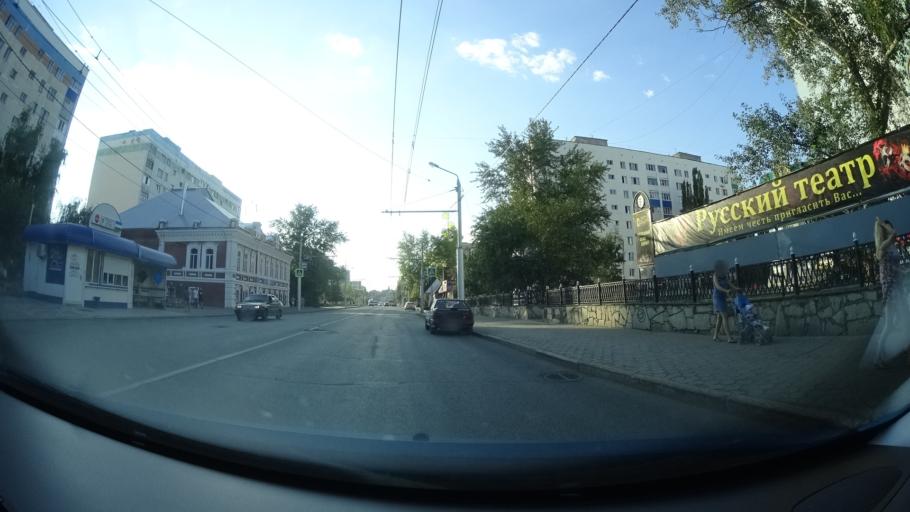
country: RU
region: Bashkortostan
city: Sterlitamak
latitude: 53.6201
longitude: 55.9597
